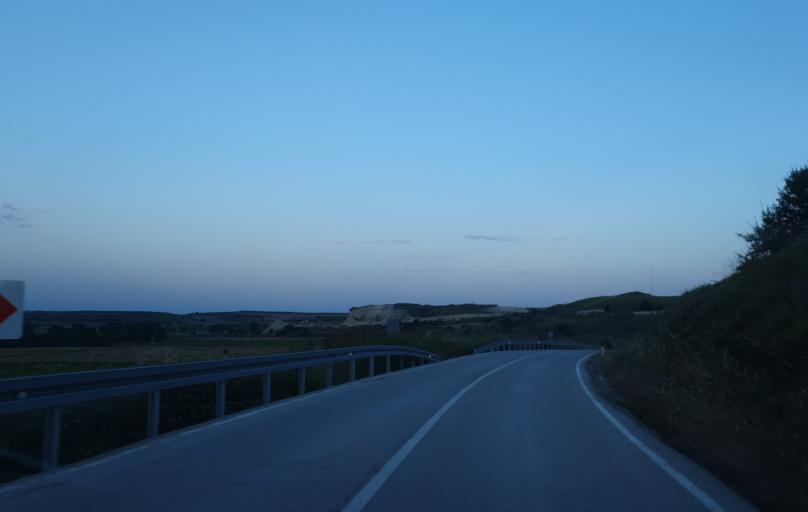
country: TR
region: Tekirdag
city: Velimese
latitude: 41.3516
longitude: 27.8575
